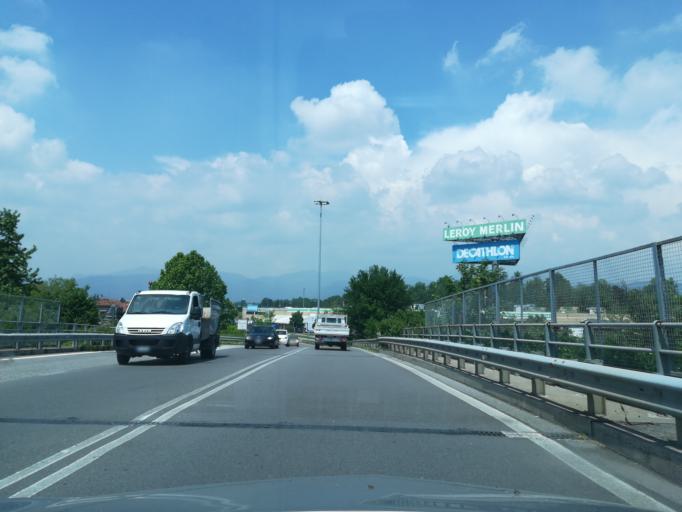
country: IT
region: Lombardy
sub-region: Provincia di Bergamo
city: Grassobbio
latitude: 45.6683
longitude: 9.7390
